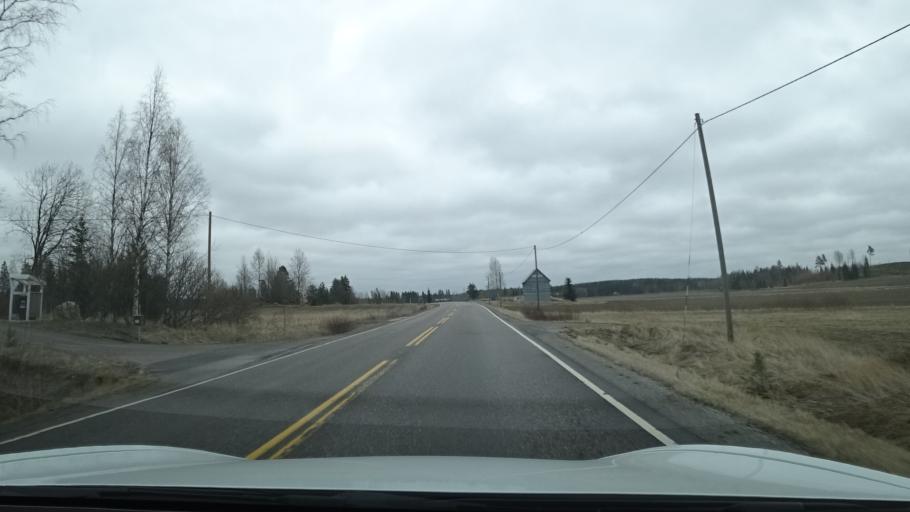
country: FI
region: Uusimaa
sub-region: Helsinki
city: Pornainen
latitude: 60.4848
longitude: 25.4382
